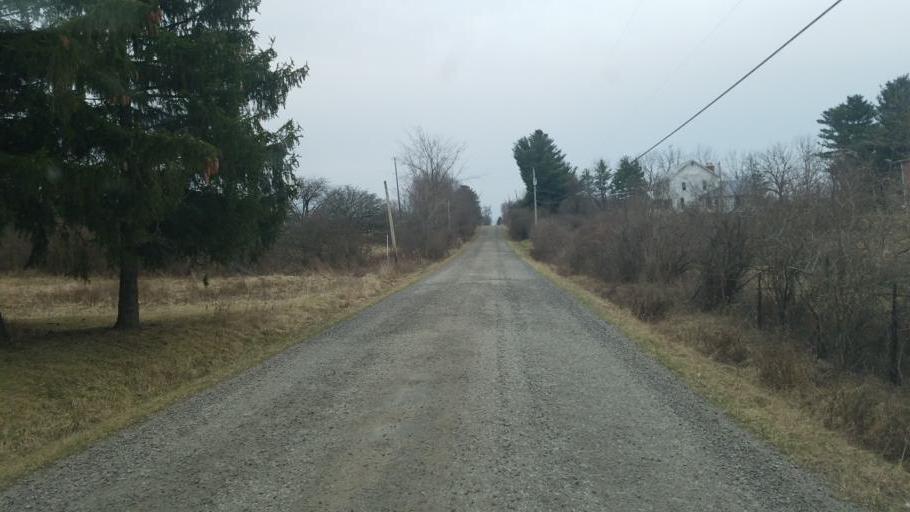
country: US
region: Ohio
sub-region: Crawford County
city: Galion
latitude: 40.6682
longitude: -82.7939
